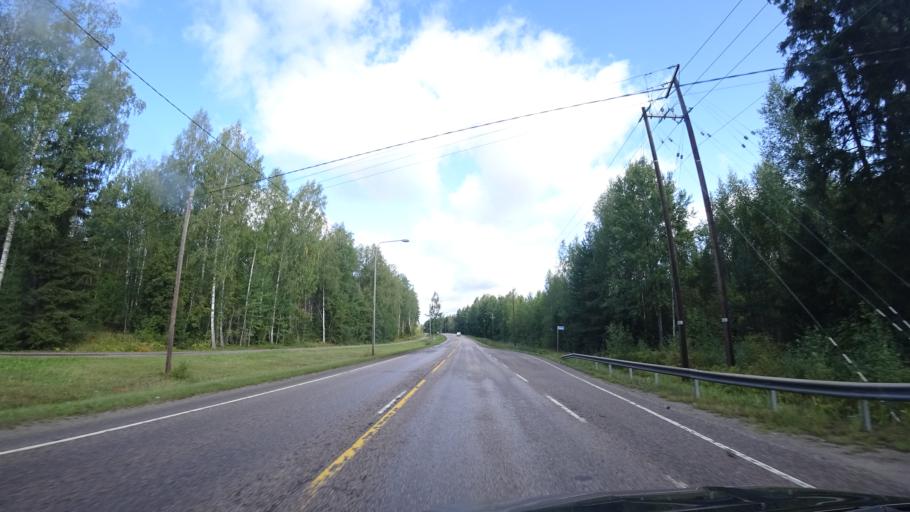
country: FI
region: Uusimaa
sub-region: Helsinki
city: Tuusula
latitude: 60.4273
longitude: 24.9956
